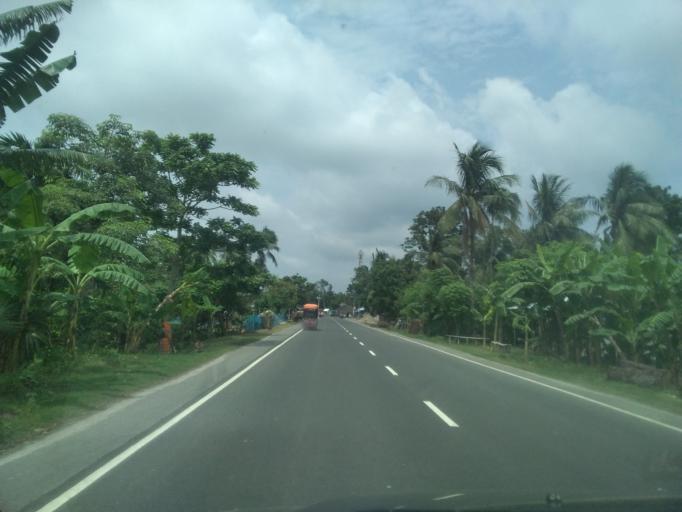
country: BD
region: Khulna
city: Kesabpur
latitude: 22.7808
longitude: 89.2056
